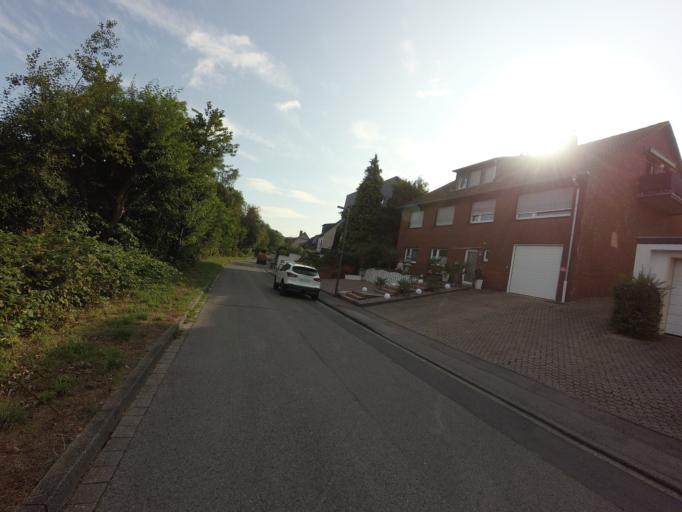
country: DE
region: North Rhine-Westphalia
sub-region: Regierungsbezirk Koln
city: Alsdorf
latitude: 50.8515
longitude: 6.1791
